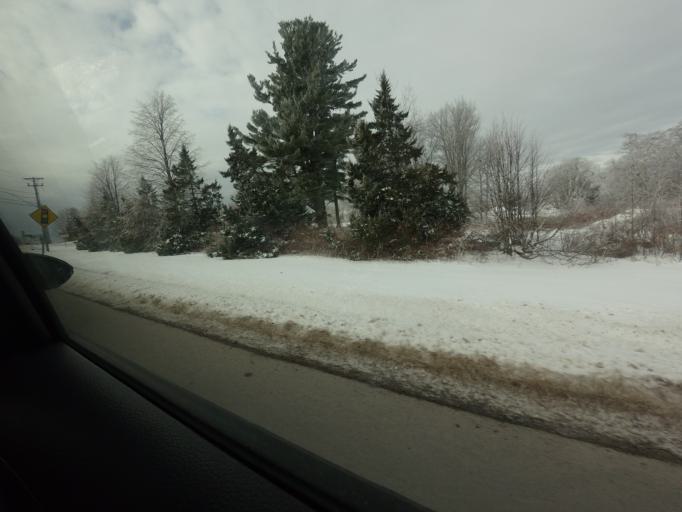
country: CA
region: New Brunswick
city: Oromocto
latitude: 45.8484
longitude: -66.4689
